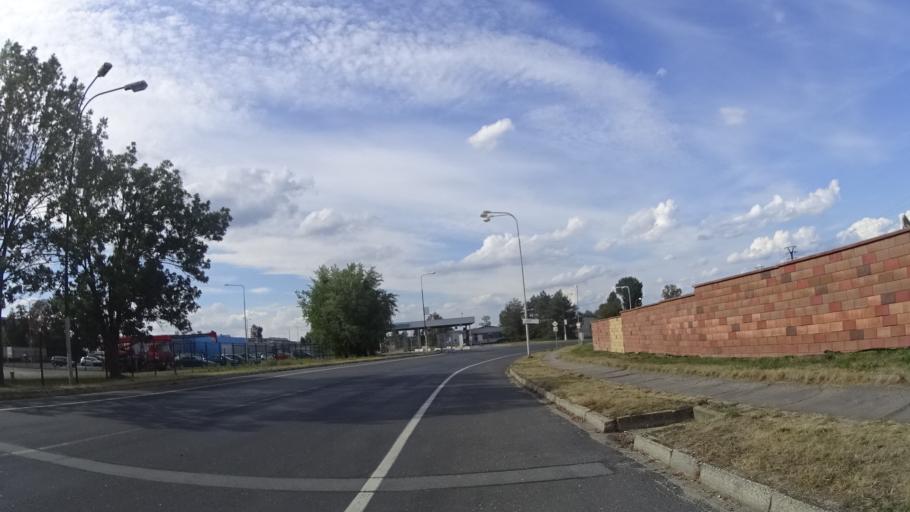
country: CZ
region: Olomoucky
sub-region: Okres Sumperk
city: Mohelnice
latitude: 49.7772
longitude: 16.9401
